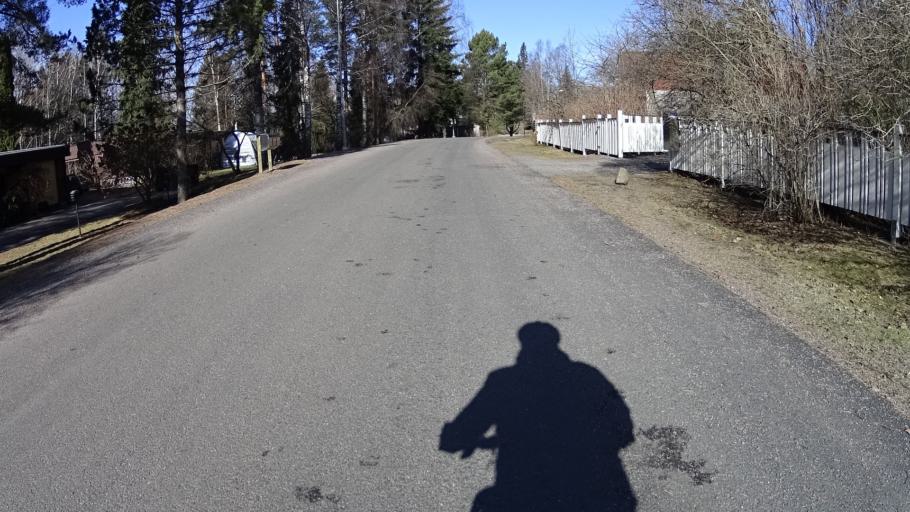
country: FI
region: Uusimaa
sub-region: Helsinki
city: Koukkuniemi
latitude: 60.1706
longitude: 24.7872
